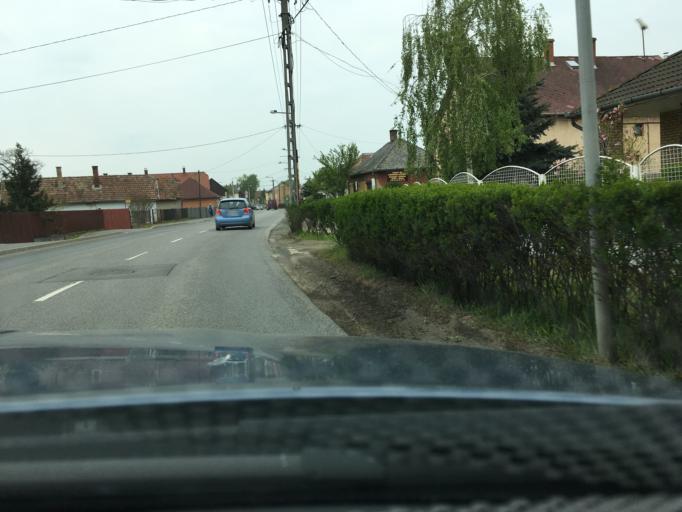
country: HU
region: Hajdu-Bihar
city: Hajdusamson
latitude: 47.6047
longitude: 21.7634
